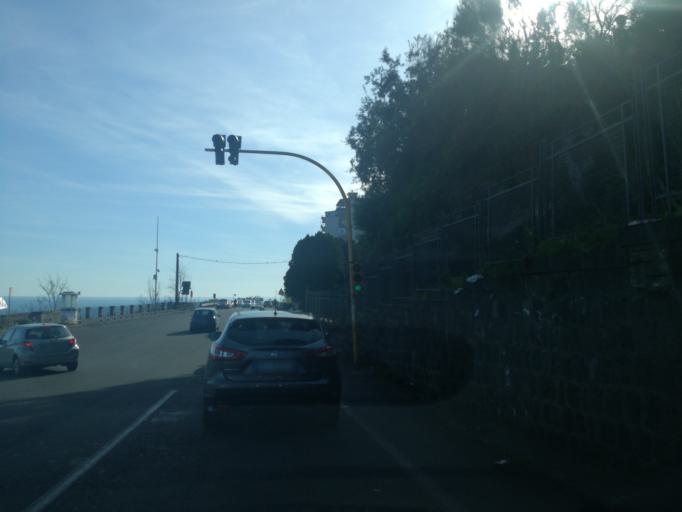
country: IT
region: Sicily
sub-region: Catania
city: Acireale
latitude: 37.6199
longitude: 15.1695
